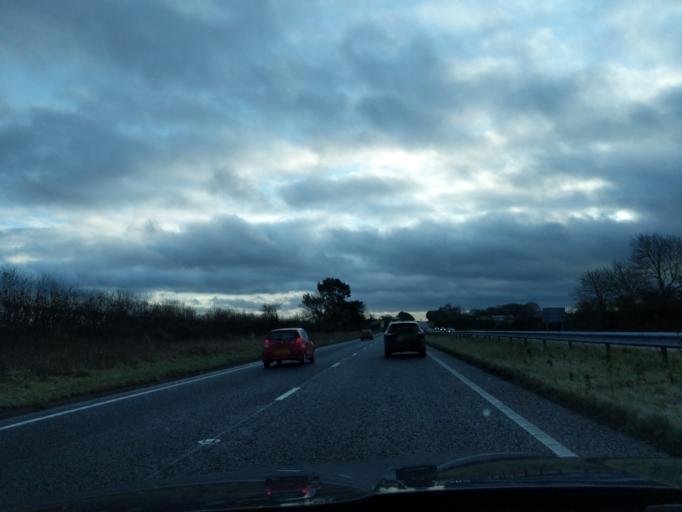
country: GB
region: England
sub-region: Northumberland
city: Felton
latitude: 55.3277
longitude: -1.7246
